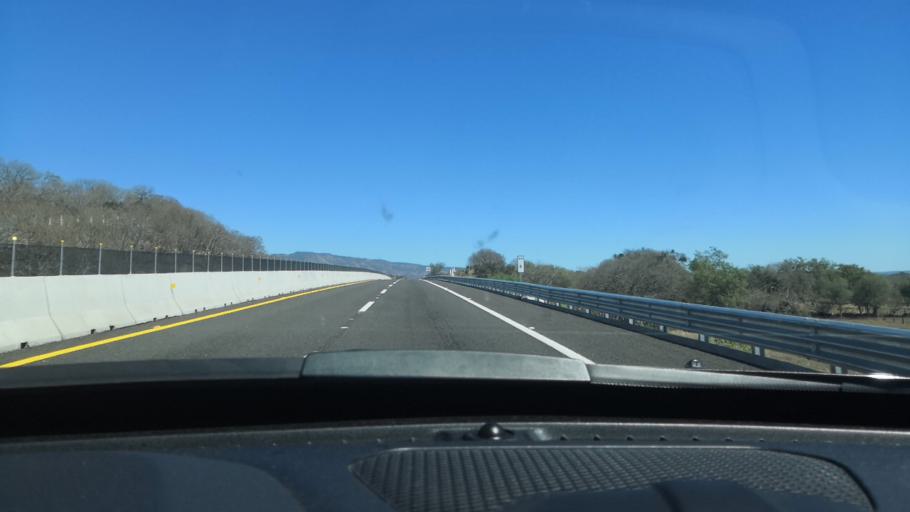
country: MX
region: Nayarit
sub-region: Ahuacatlan
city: Ahuacatlan
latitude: 21.0662
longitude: -104.4833
